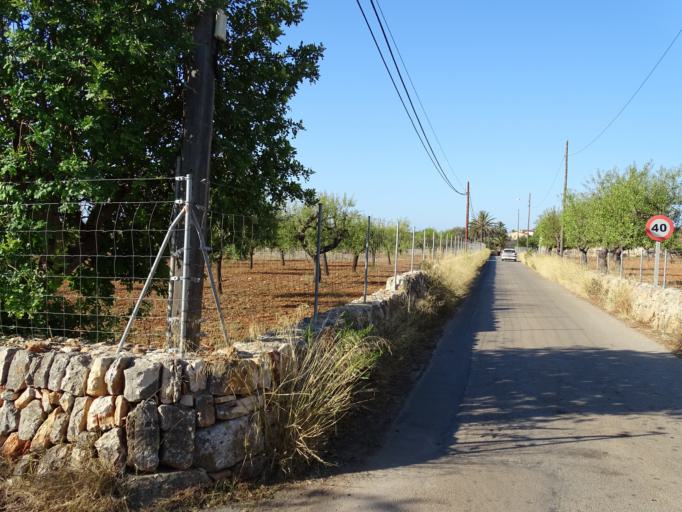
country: ES
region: Balearic Islands
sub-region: Illes Balears
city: Felanitx
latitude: 39.4029
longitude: 3.2104
